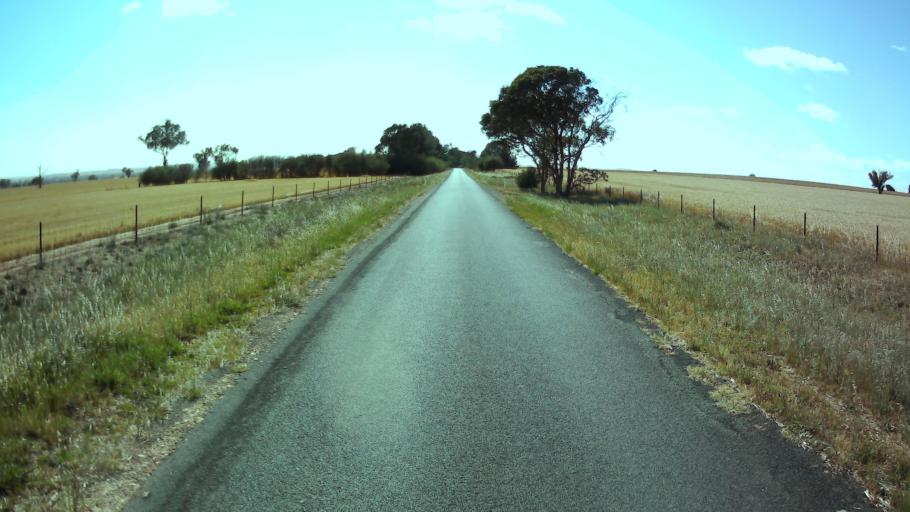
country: AU
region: New South Wales
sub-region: Weddin
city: Grenfell
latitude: -34.0619
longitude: 148.2575
